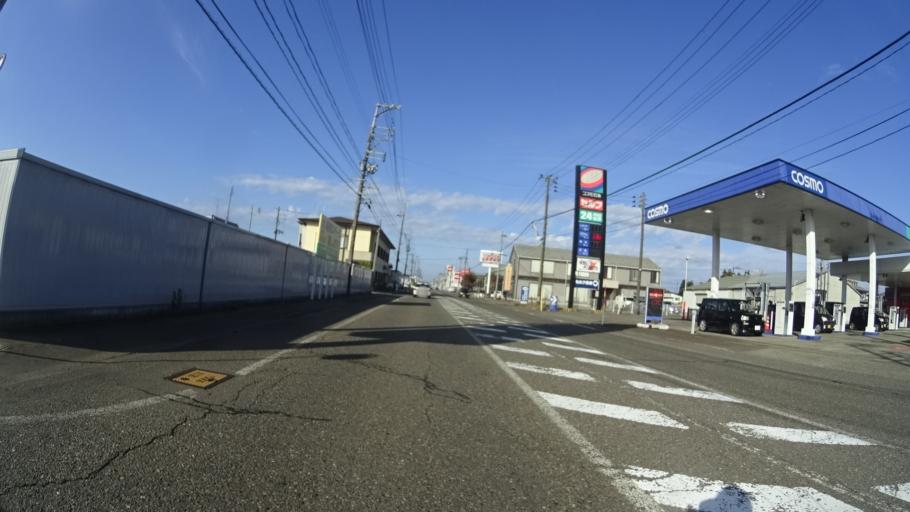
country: JP
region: Niigata
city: Joetsu
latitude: 37.1550
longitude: 138.2382
